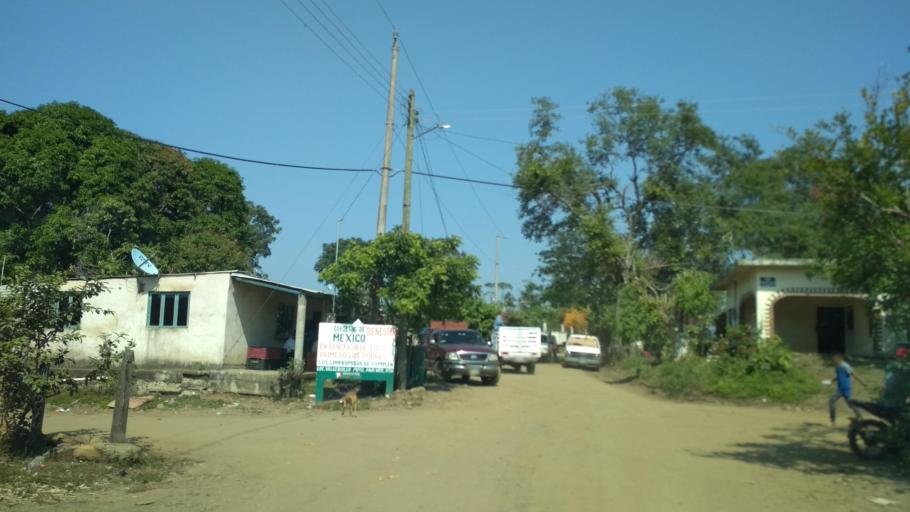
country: MX
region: Puebla
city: San Jose Acateno
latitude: 20.1766
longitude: -97.2334
